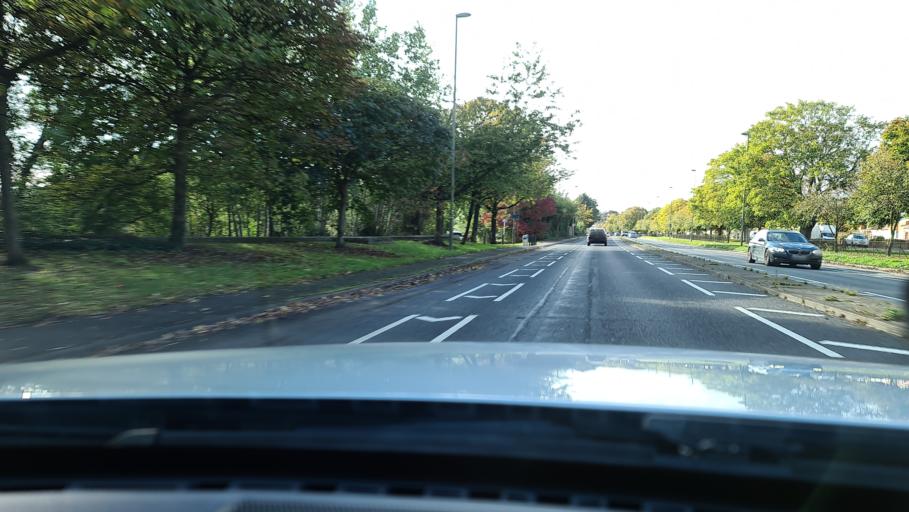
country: GB
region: England
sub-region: Surrey
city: Esher
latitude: 51.3688
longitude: -0.3882
